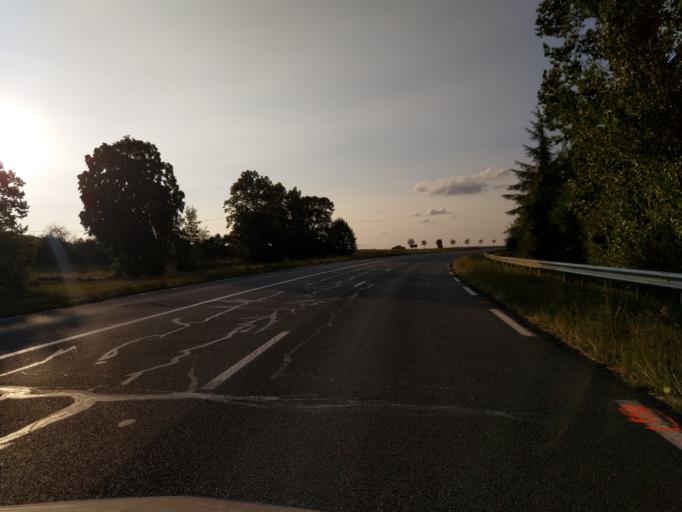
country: FR
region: Midi-Pyrenees
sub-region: Departement du Tarn
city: Realmont
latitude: 43.8016
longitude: 2.1841
